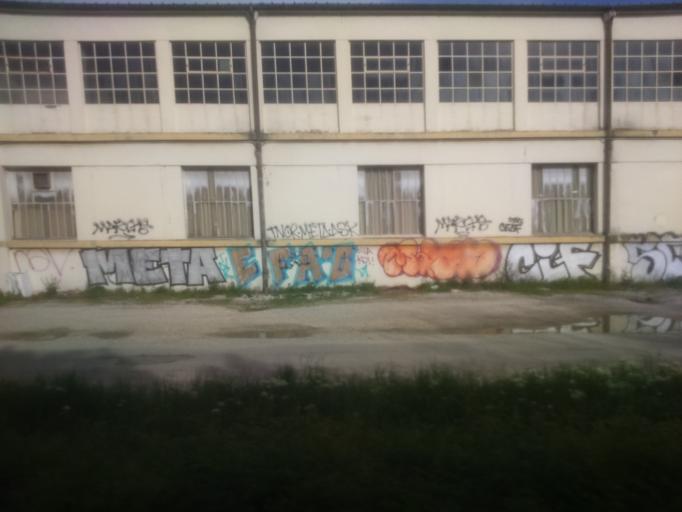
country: FR
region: Rhone-Alpes
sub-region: Departement de l'Isere
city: Le Pont-de-Claix
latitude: 45.1387
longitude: 5.7034
